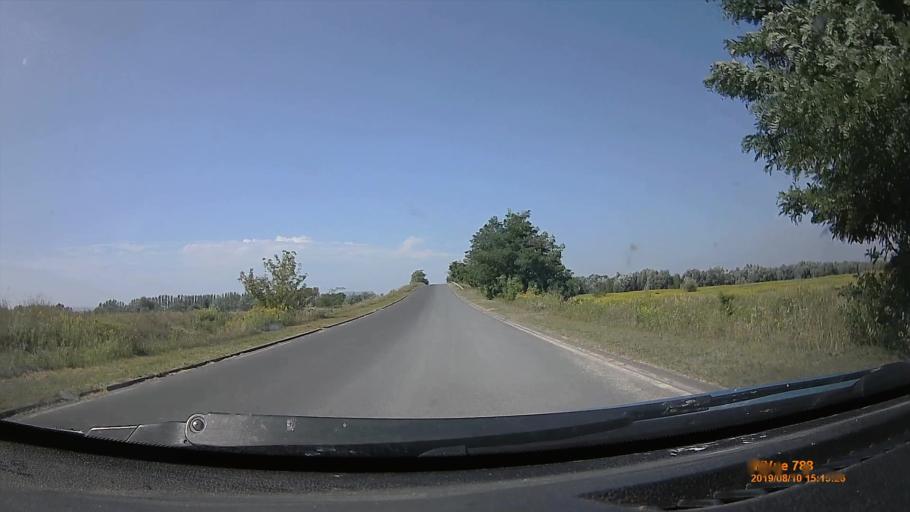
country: HU
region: Somogy
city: Fonyod
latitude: 46.6990
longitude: 17.5574
